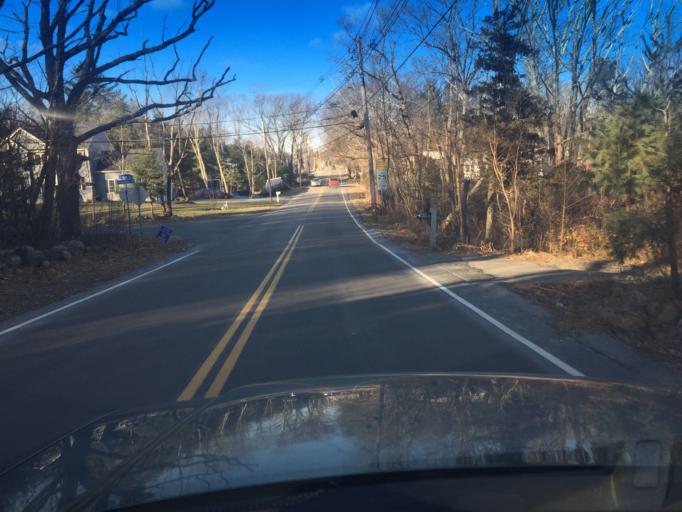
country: US
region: Massachusetts
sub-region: Middlesex County
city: Holliston
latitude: 42.1782
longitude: -71.4114
